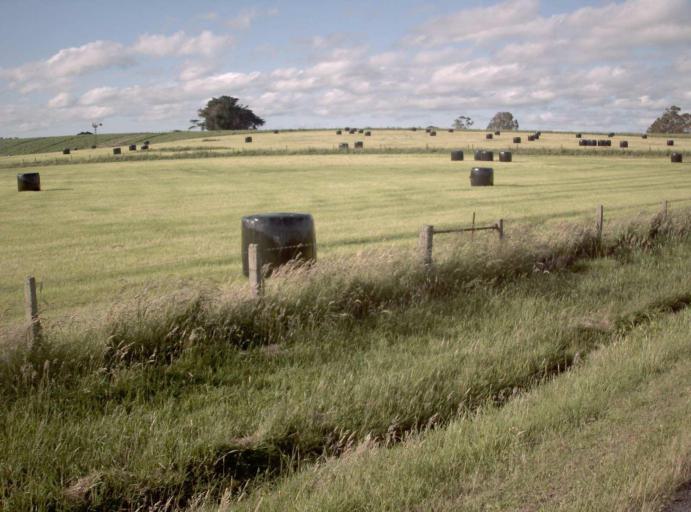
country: AU
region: Victoria
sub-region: Bass Coast
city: North Wonthaggi
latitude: -38.5002
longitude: 145.9188
